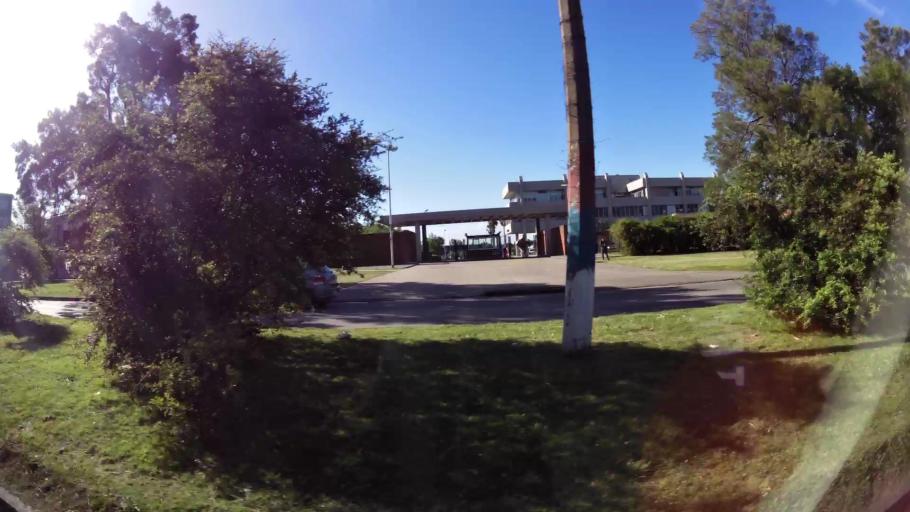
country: UY
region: Canelones
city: Paso de Carrasco
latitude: -34.8806
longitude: -56.0764
